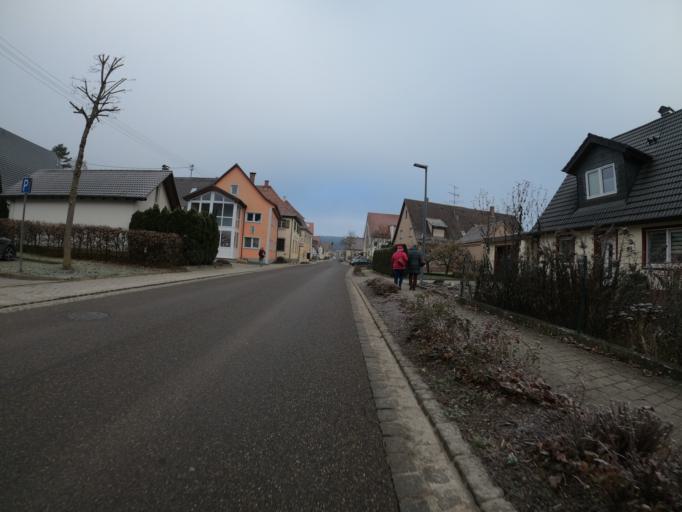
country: DE
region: Baden-Wuerttemberg
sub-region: Tuebingen Region
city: Westerstetten
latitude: 48.5186
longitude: 9.9538
